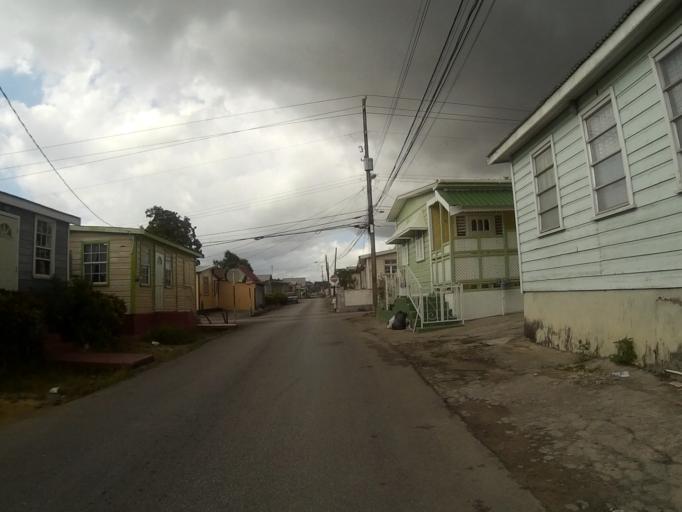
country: BB
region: Saint Michael
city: Bridgetown
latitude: 13.1011
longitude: -59.6039
